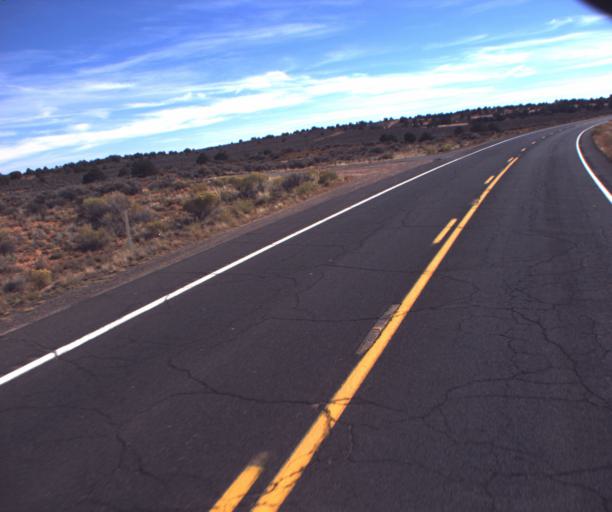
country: US
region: Arizona
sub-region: Coconino County
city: Kaibito
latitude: 36.5768
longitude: -110.7740
